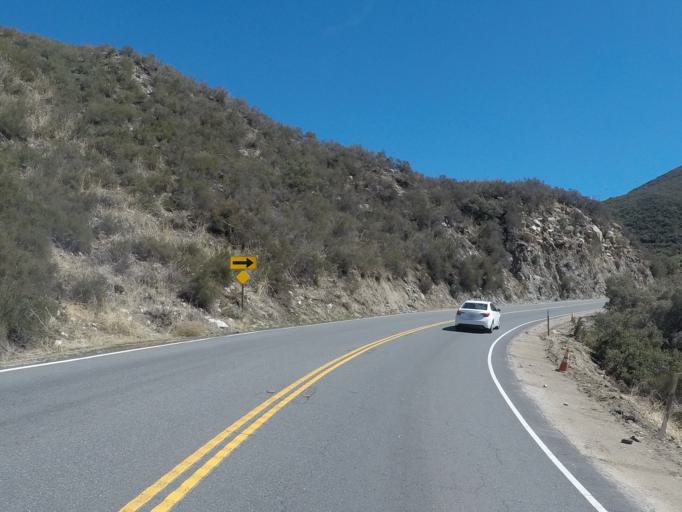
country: US
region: California
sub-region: Riverside County
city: Idyllwild-Pine Cove
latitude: 33.7077
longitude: -116.7567
